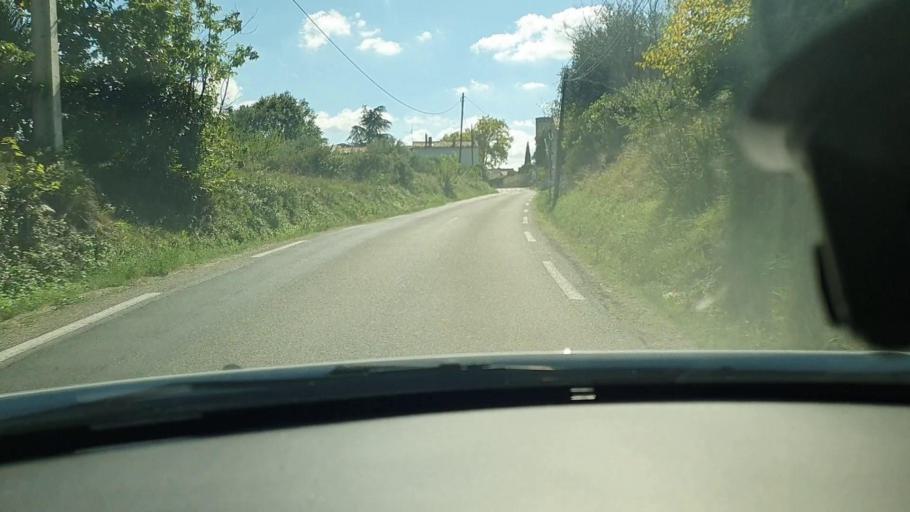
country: FR
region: Languedoc-Roussillon
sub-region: Departement du Gard
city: Goudargues
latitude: 44.1646
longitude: 4.4850
